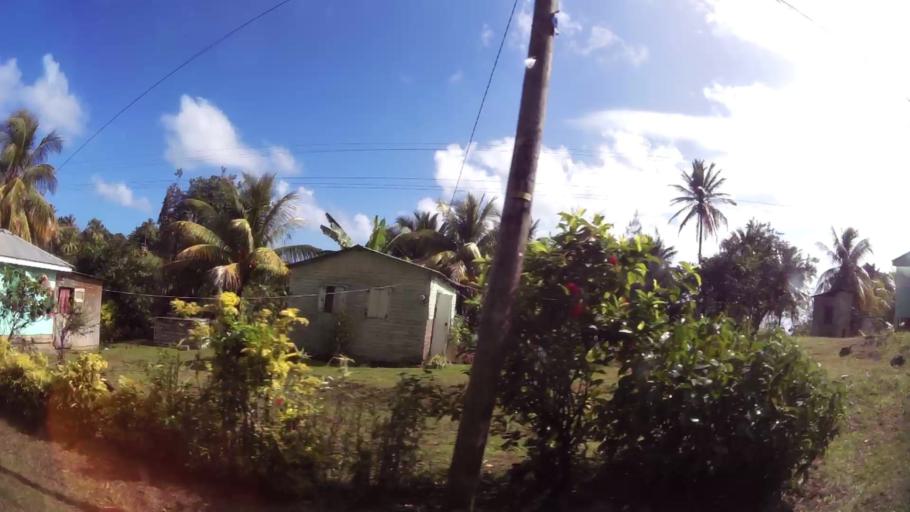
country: DM
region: Saint David
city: Castle Bruce
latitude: 15.4707
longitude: -61.2492
